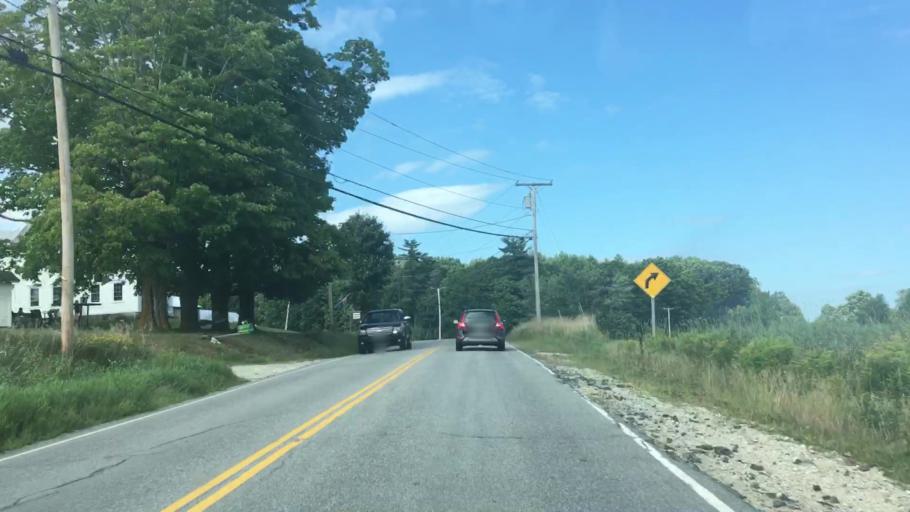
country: US
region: Maine
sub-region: Oxford County
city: Oxford
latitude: 44.1294
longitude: -70.5033
